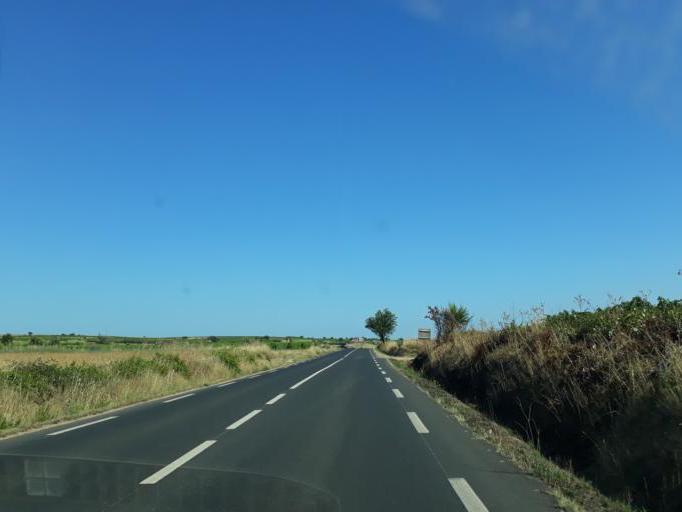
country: FR
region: Languedoc-Roussillon
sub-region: Departement de l'Herault
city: Florensac
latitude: 43.3641
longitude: 3.4853
